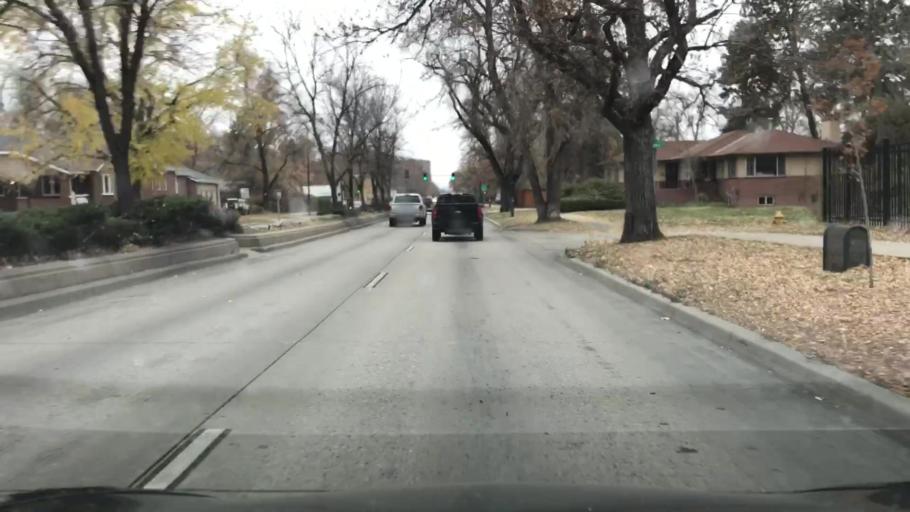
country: US
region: Colorado
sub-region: Arapahoe County
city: Glendale
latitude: 39.6785
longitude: -104.9491
